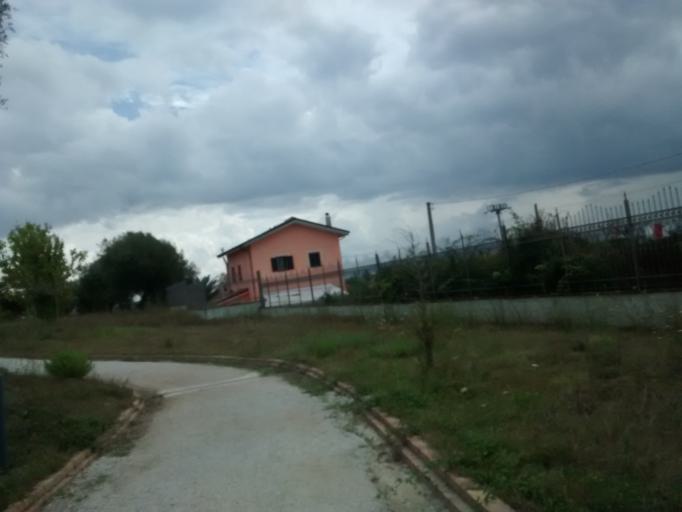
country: IT
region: Calabria
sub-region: Provincia di Vibo-Valentia
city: Vibo Valentia
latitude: 38.6627
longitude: 16.0788
